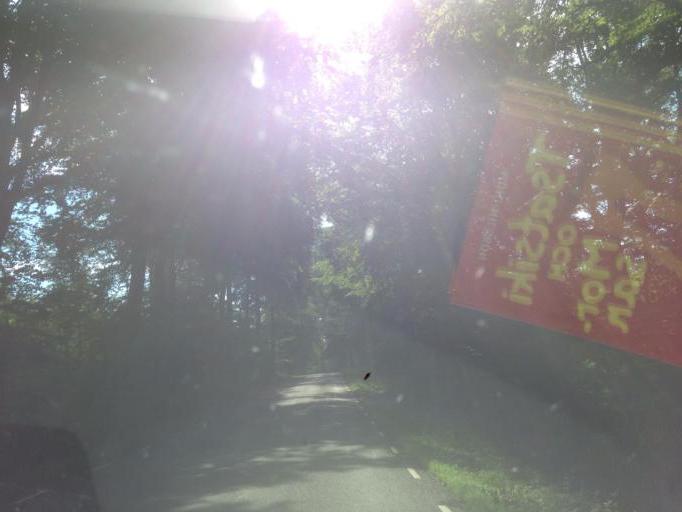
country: SE
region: Skane
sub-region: Tomelilla Kommun
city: Tomelilla
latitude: 55.6436
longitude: 14.0499
